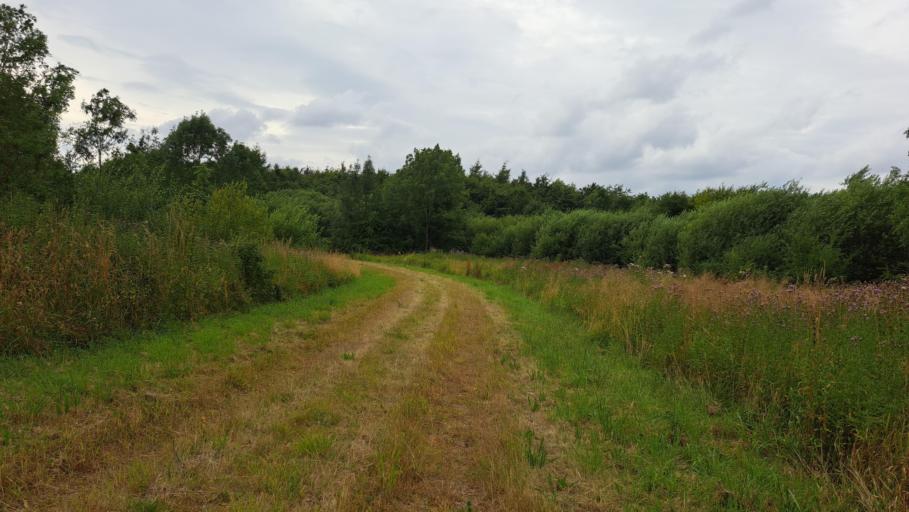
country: DK
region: Central Jutland
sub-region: Hedensted Kommune
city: Hedensted
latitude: 55.8033
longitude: 9.7162
